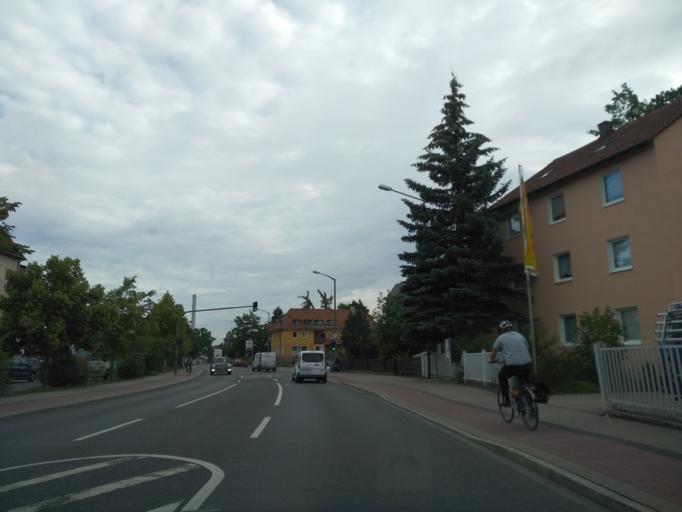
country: DE
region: Bavaria
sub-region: Regierungsbezirk Mittelfranken
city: Erlangen
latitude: 49.5827
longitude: 11.0059
